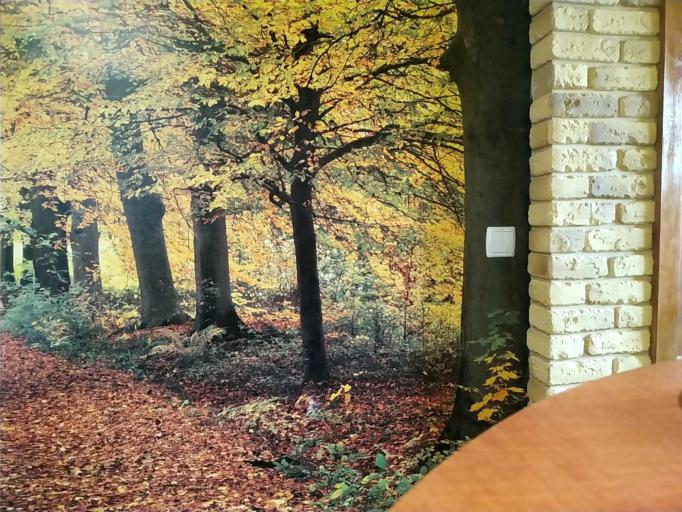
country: RU
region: Novgorod
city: Opechenskiy Posad
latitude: 58.2700
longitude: 34.0121
